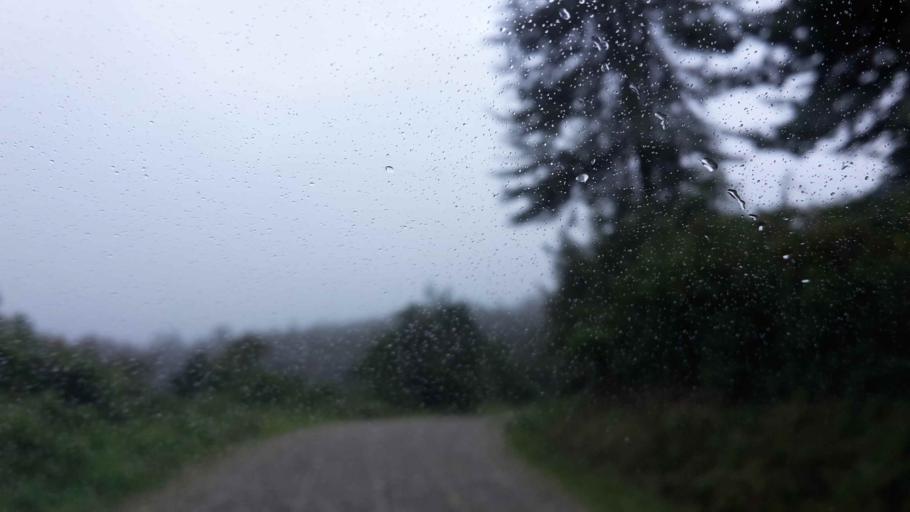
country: BO
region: Cochabamba
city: Colomi
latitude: -17.1658
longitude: -65.8997
